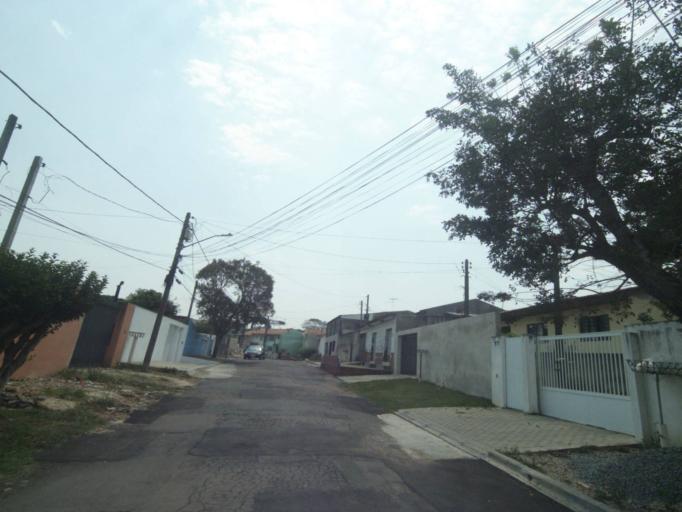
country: BR
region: Parana
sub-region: Sao Jose Dos Pinhais
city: Sao Jose dos Pinhais
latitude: -25.5392
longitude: -49.2457
